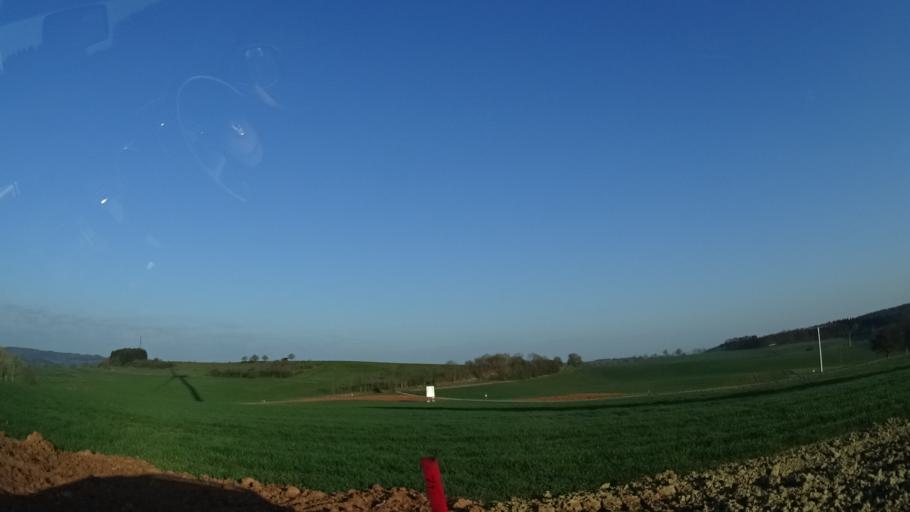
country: DE
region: Rheinland-Pfalz
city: Hoppstadten
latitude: 49.6863
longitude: 7.5198
